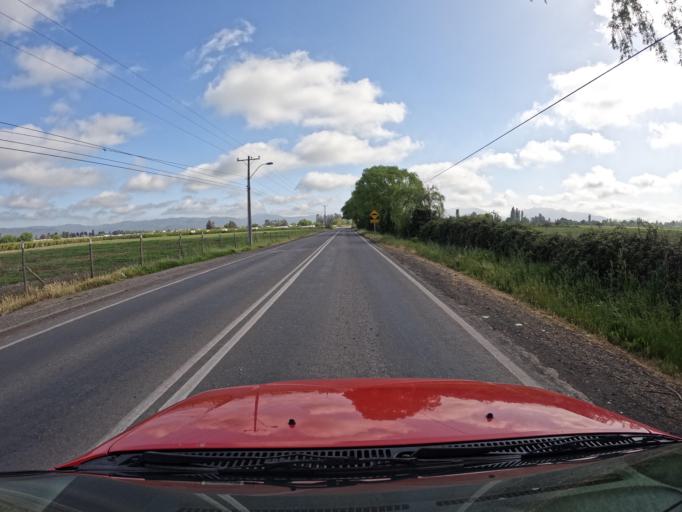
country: CL
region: Maule
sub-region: Provincia de Curico
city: Rauco
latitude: -34.8925
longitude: -71.2739
